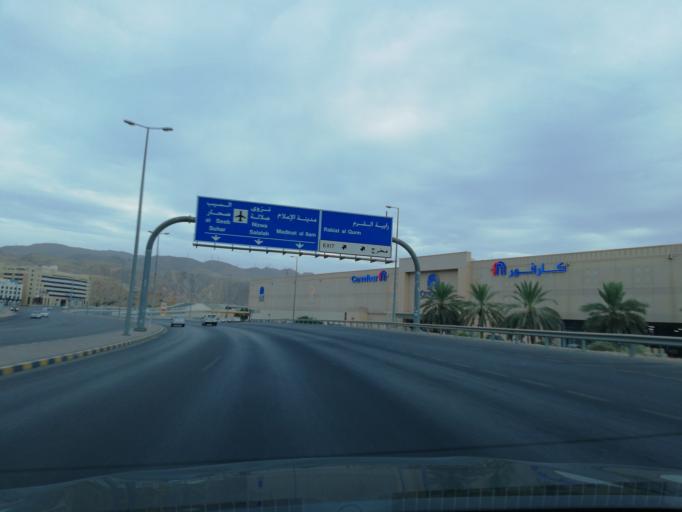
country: OM
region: Muhafazat Masqat
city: Muscat
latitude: 23.6094
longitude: 58.4914
